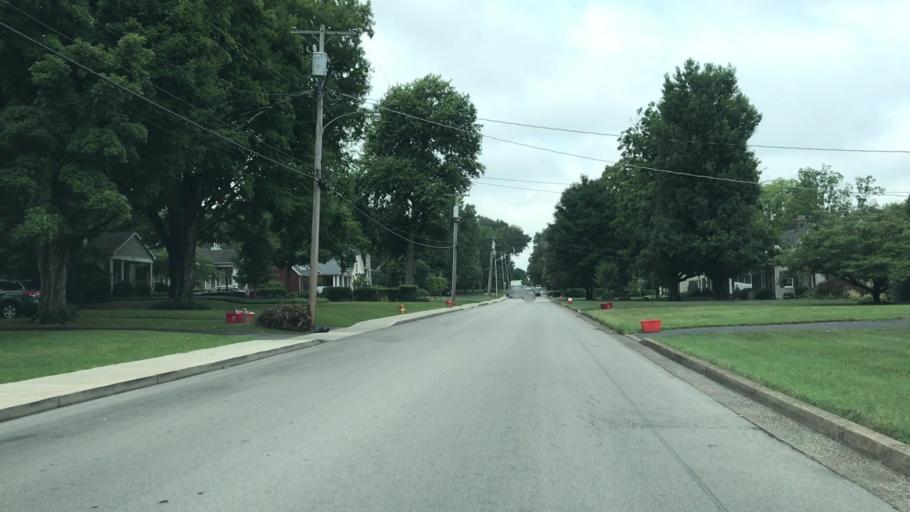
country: US
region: Kentucky
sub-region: Warren County
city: Bowling Green
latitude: 36.9819
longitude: -86.4291
